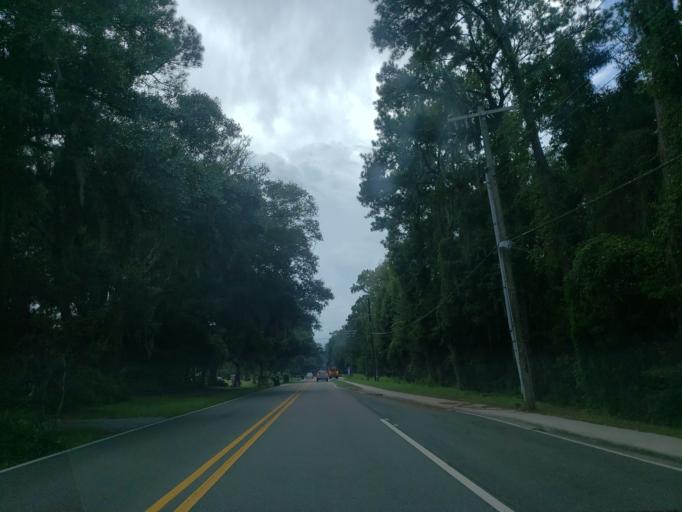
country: US
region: Georgia
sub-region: Chatham County
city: Wilmington Island
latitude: 32.0058
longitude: -80.9712
